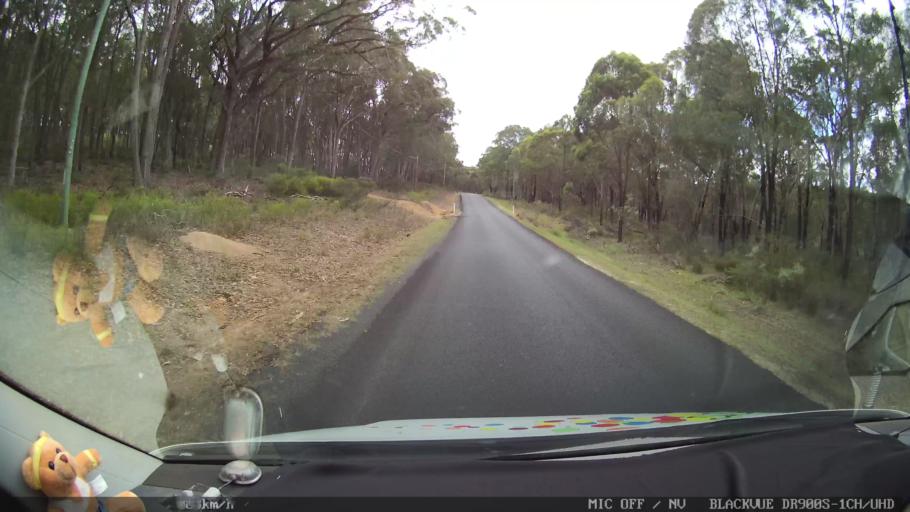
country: AU
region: New South Wales
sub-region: Glen Innes Severn
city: Glen Innes
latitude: -29.4346
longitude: 151.6321
